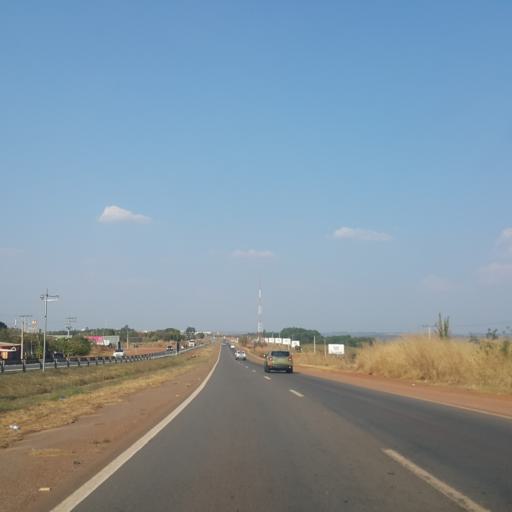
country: BR
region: Goias
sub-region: Abadiania
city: Abadiania
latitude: -16.1214
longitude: -48.4253
